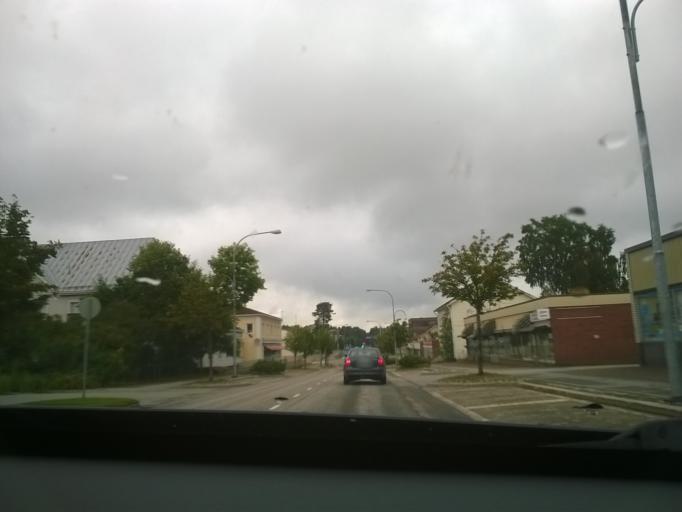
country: FI
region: Kainuu
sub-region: Kehys-Kainuu
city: Kuhmo
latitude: 64.1262
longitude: 29.5155
